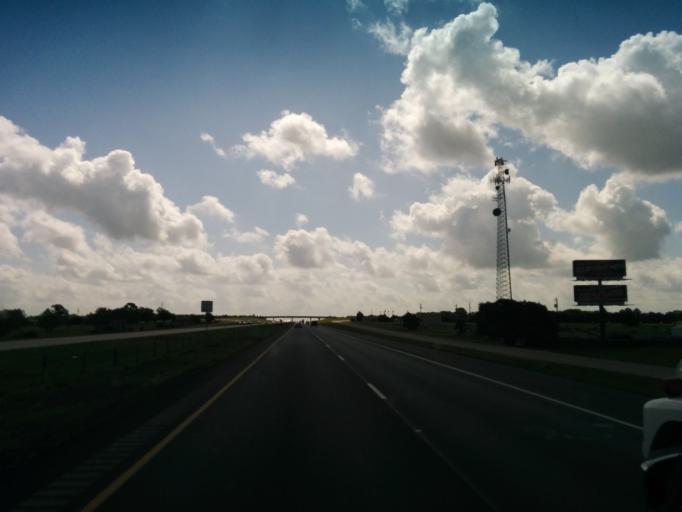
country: US
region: Texas
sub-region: Colorado County
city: Weimar
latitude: 29.6921
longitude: -96.7549
